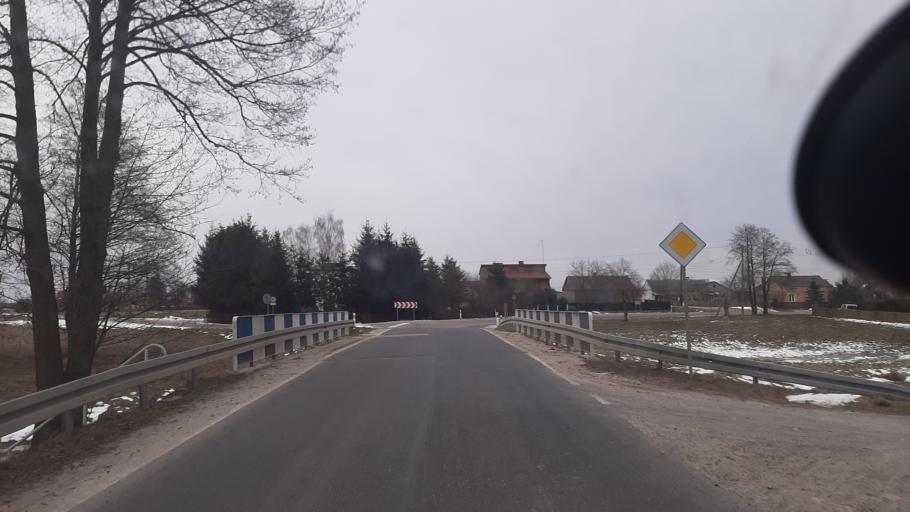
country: PL
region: Lublin Voivodeship
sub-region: Powiat lubartowski
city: Kamionka
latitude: 51.4681
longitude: 22.4182
